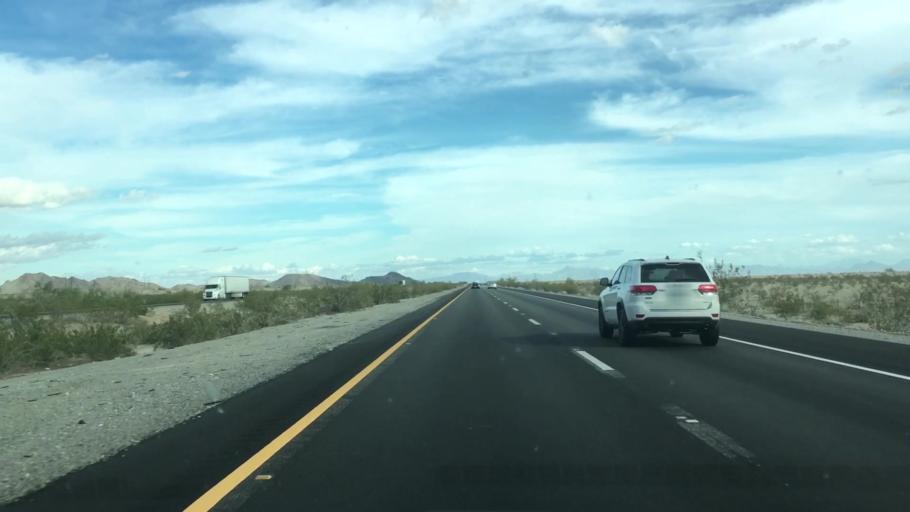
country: US
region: California
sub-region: Riverside County
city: Mesa Verde
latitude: 33.6096
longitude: -114.8245
